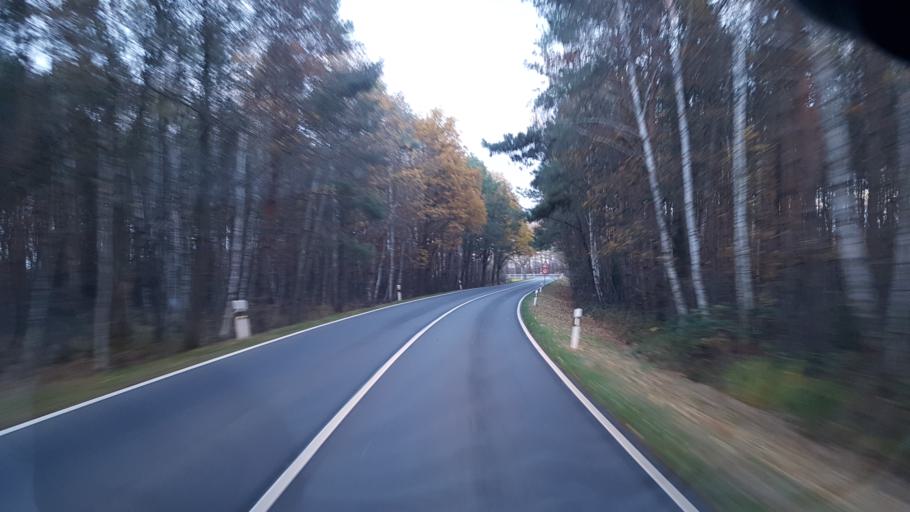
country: DE
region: Brandenburg
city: Schraden
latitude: 51.4428
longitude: 13.7077
